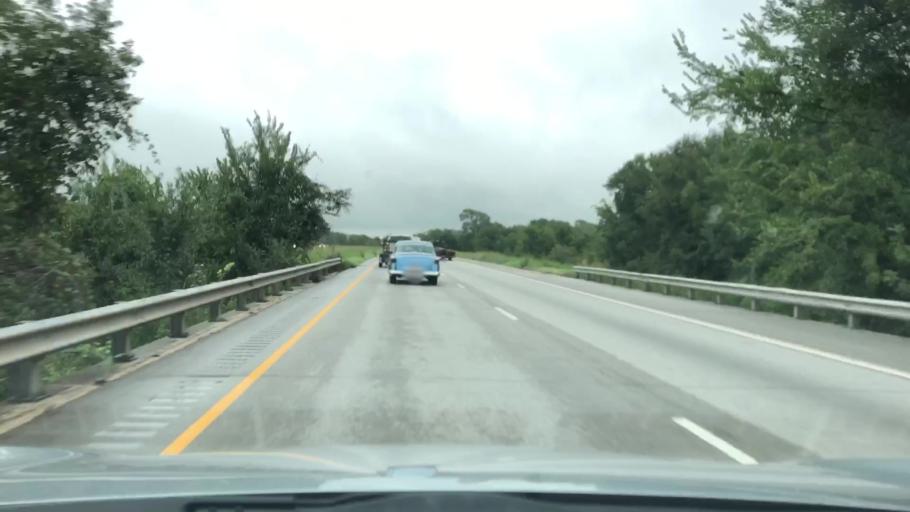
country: US
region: Texas
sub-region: Fayette County
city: Flatonia
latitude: 29.6919
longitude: -97.1888
